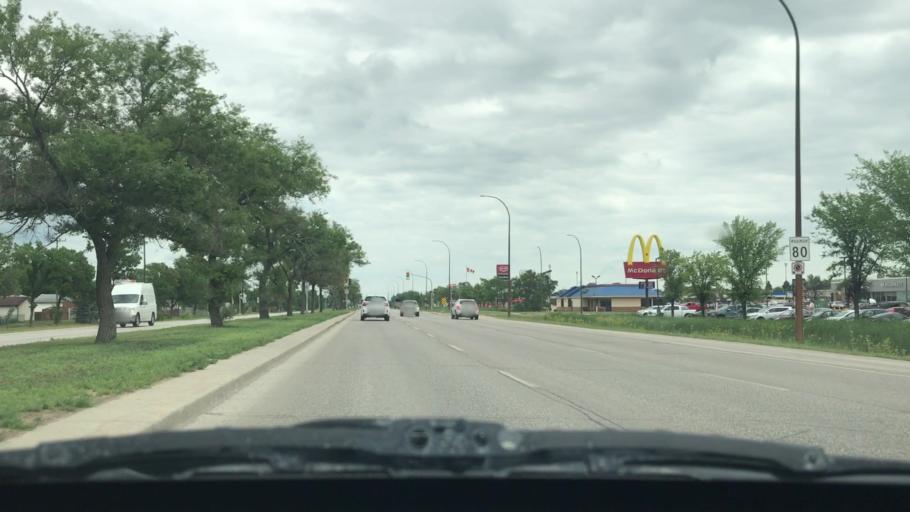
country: CA
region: Manitoba
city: Winnipeg
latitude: 49.8560
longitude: -97.0764
